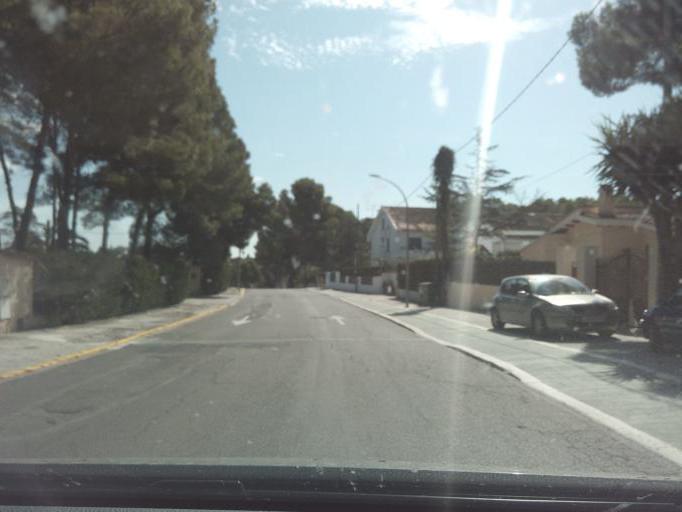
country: ES
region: Valencia
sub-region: Provincia de Valencia
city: Betera
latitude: 39.5412
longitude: -0.4814
